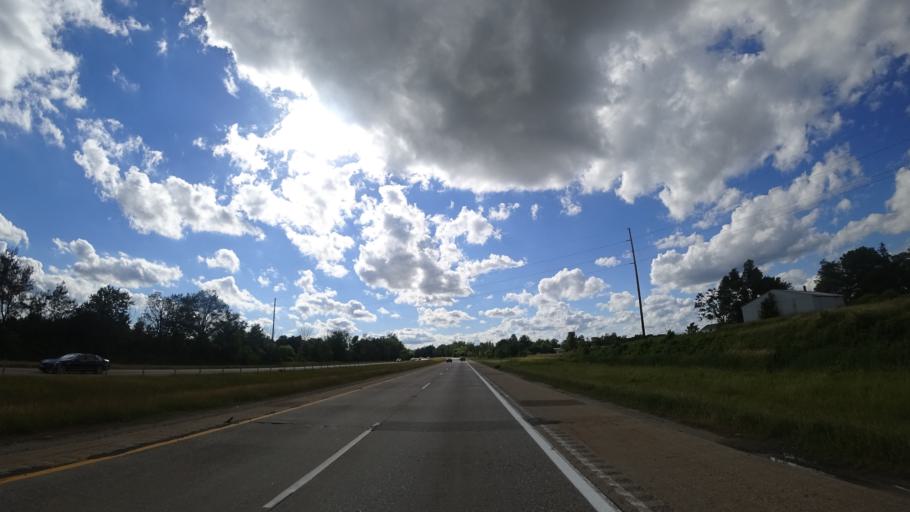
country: US
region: Michigan
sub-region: Ionia County
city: Portland
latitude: 42.8772
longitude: -84.9717
